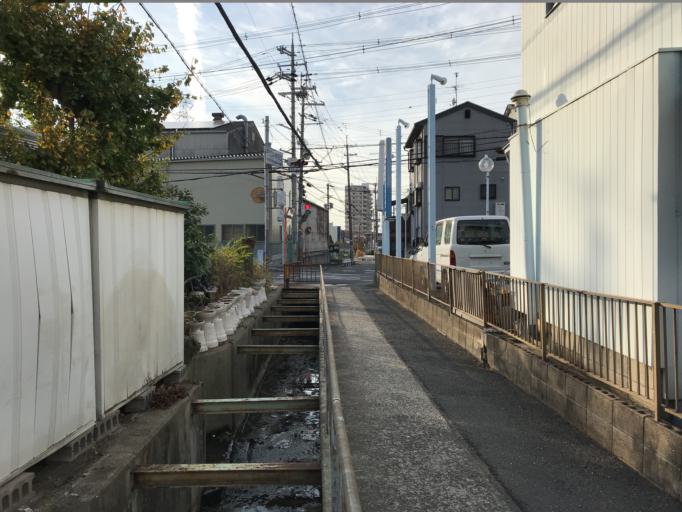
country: JP
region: Osaka
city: Daitocho
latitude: 34.6894
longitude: 135.6442
